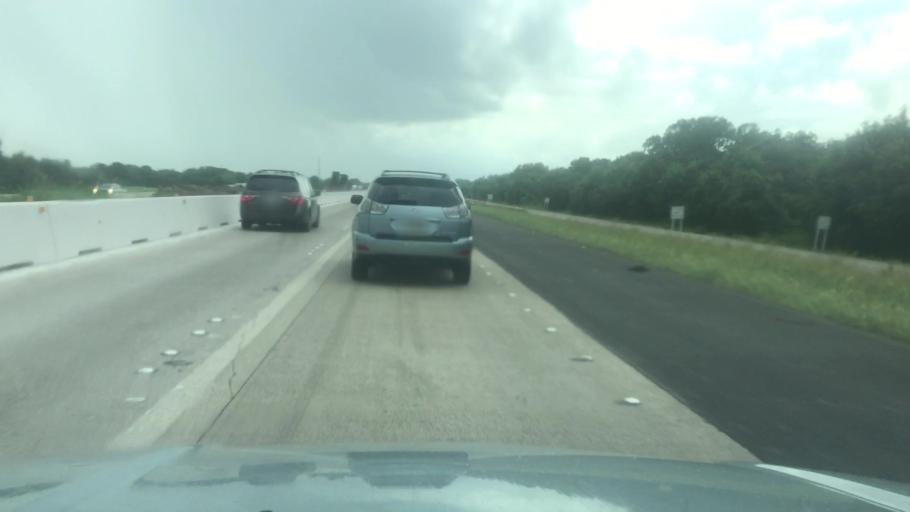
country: US
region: Texas
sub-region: Waller County
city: Brookshire
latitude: 29.7756
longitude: -96.0178
